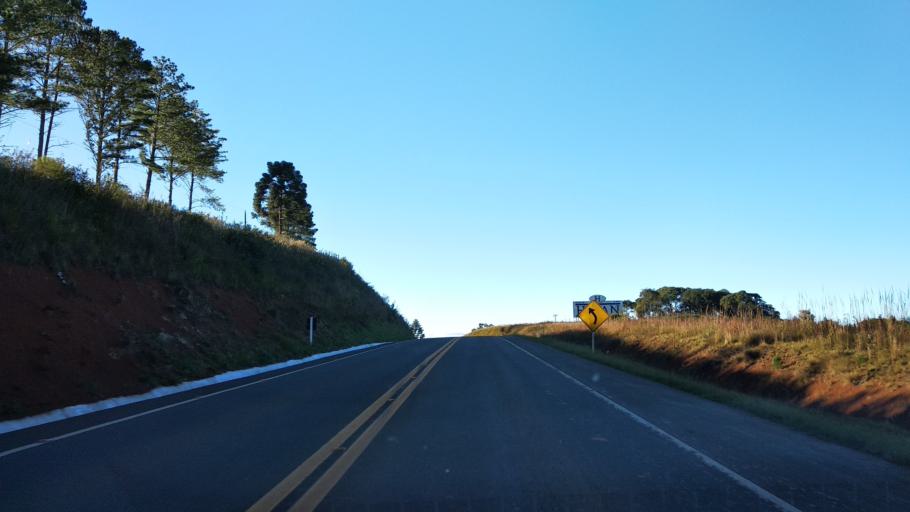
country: BR
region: Santa Catarina
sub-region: Lages
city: Lages
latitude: -27.7916
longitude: -50.4077
